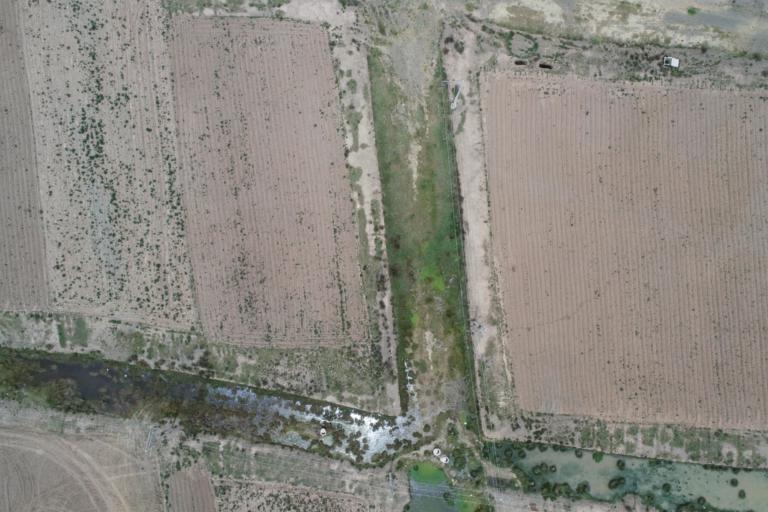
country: BO
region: La Paz
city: La Paz
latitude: -16.5170
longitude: -68.3006
